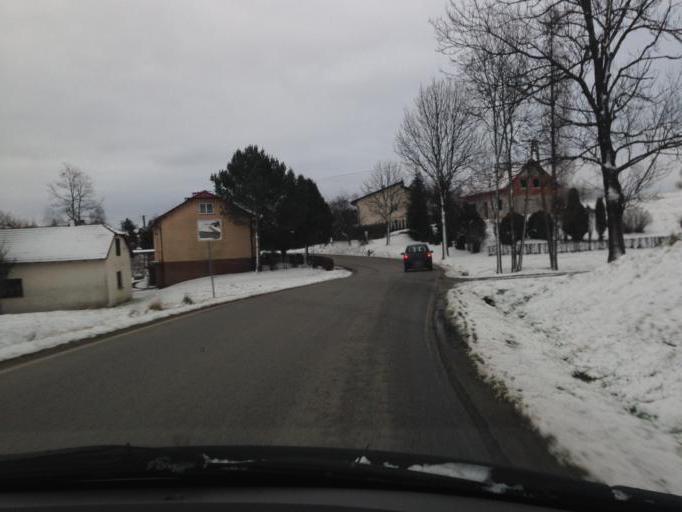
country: PL
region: Lesser Poland Voivodeship
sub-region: Powiat gorlicki
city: Moszczenica
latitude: 49.7407
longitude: 21.0855
